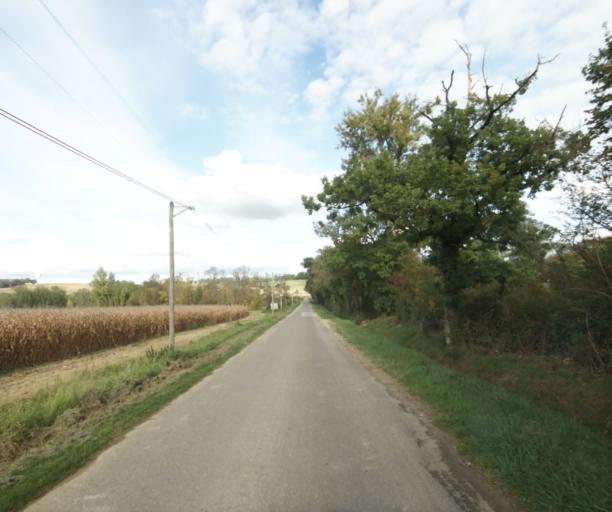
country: FR
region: Midi-Pyrenees
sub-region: Departement du Gers
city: Gondrin
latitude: 43.8703
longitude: 0.2164
